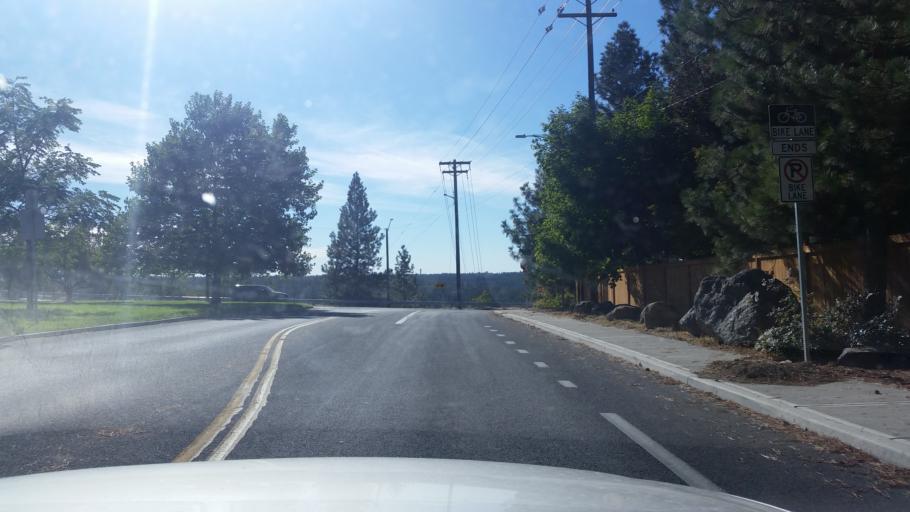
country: US
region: Washington
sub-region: Spokane County
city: Spokane
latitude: 47.6282
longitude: -117.4281
